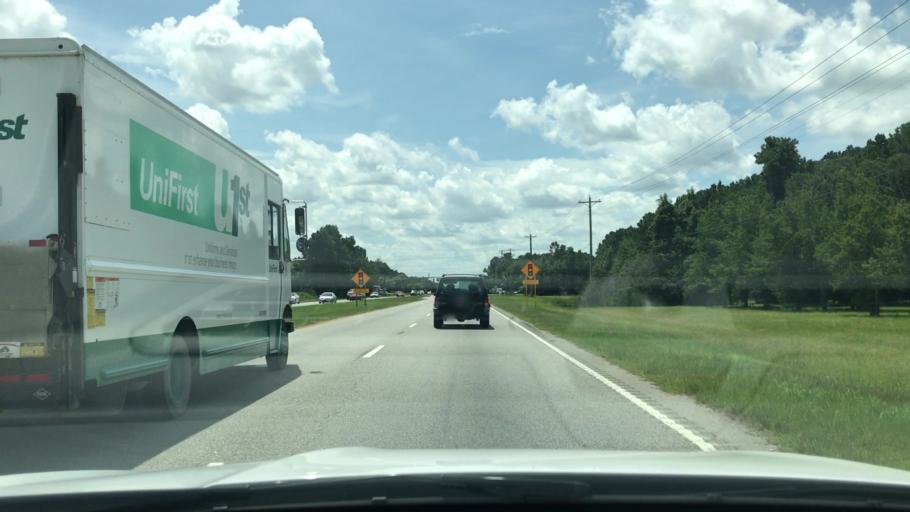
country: US
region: South Carolina
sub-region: Berkeley County
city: Goose Creek
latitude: 33.0360
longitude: -80.0341
